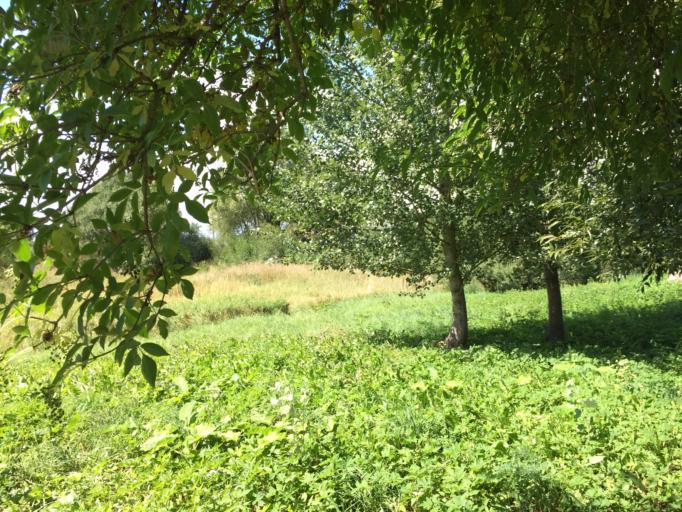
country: LV
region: Rundales
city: Pilsrundale
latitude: 56.3236
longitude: 23.9182
